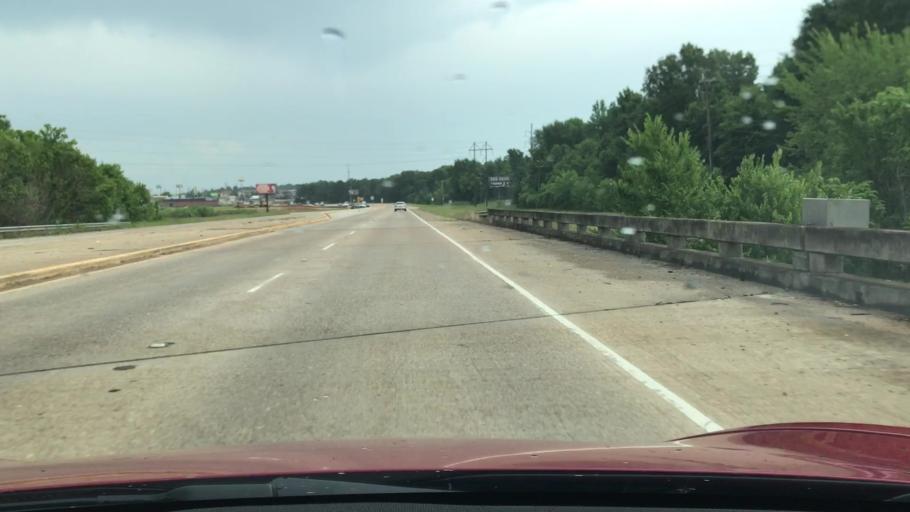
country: US
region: Louisiana
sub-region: Bossier Parish
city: Bossier City
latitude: 32.3999
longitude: -93.7723
